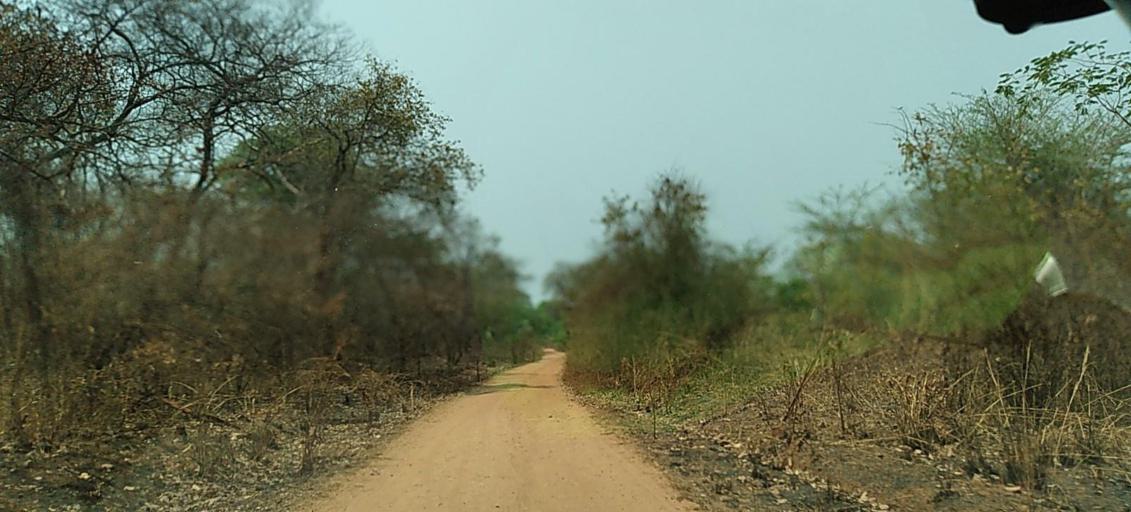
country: ZM
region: North-Western
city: Kabompo
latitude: -13.7052
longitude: 24.3219
